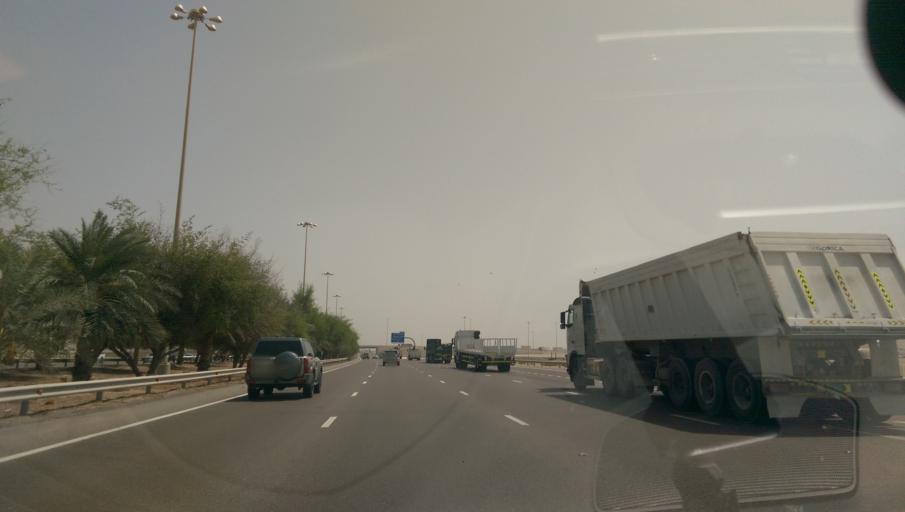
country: AE
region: Abu Dhabi
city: Abu Dhabi
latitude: 24.3631
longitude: 54.6517
